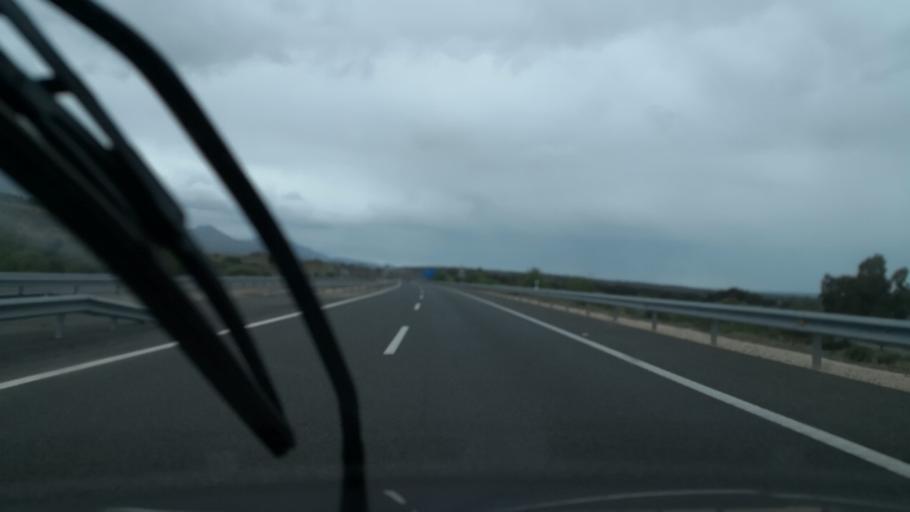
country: ES
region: Extremadura
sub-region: Provincia de Caceres
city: Casas del Monte
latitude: 40.2203
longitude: -5.9844
